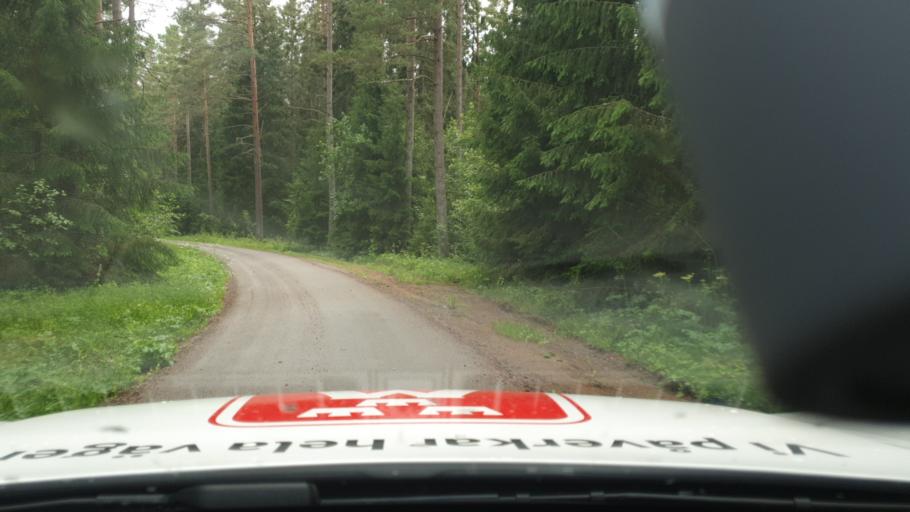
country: SE
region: Vaestra Goetaland
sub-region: Falkopings Kommun
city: Falkoeping
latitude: 58.0485
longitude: 13.6607
